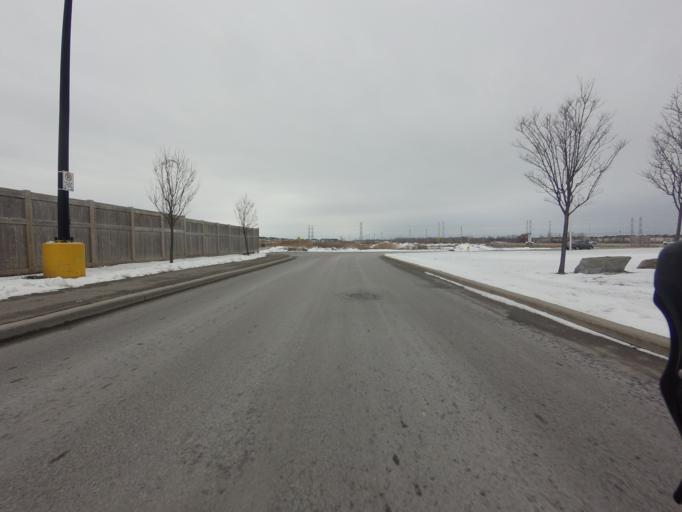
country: CA
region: Ontario
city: Bells Corners
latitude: 45.2749
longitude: -75.8737
